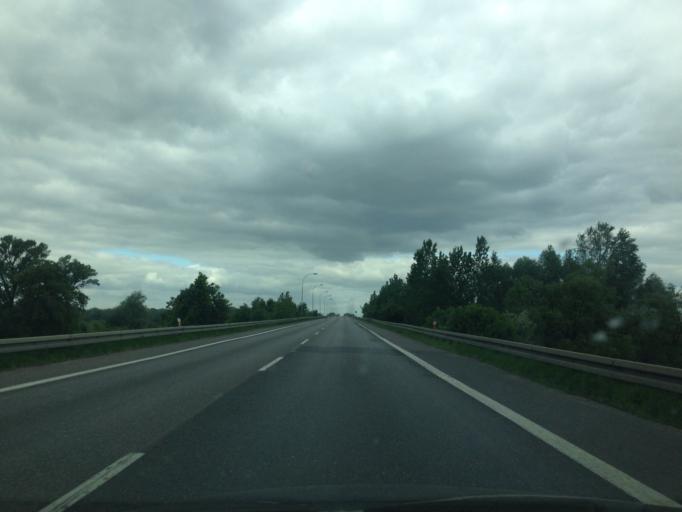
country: PL
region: Kujawsko-Pomorskie
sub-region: Powiat chelminski
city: Chelmno
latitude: 53.3639
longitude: 18.4339
